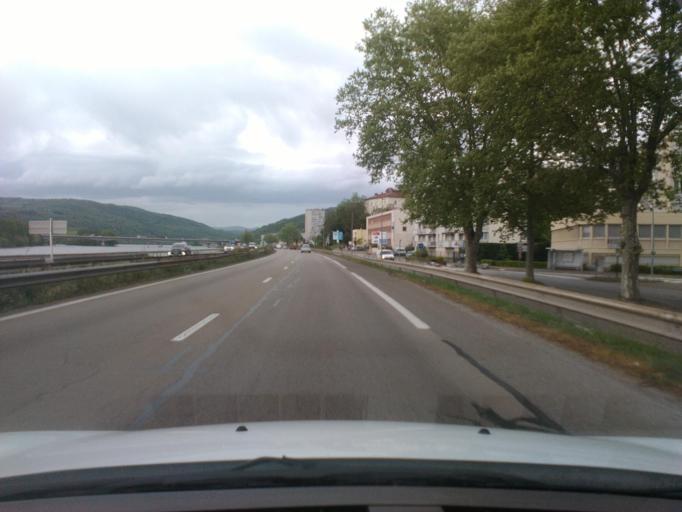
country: FR
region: Rhone-Alpes
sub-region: Departement du Rhone
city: Saint-Romain-en-Gal
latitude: 45.5371
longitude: 4.8682
